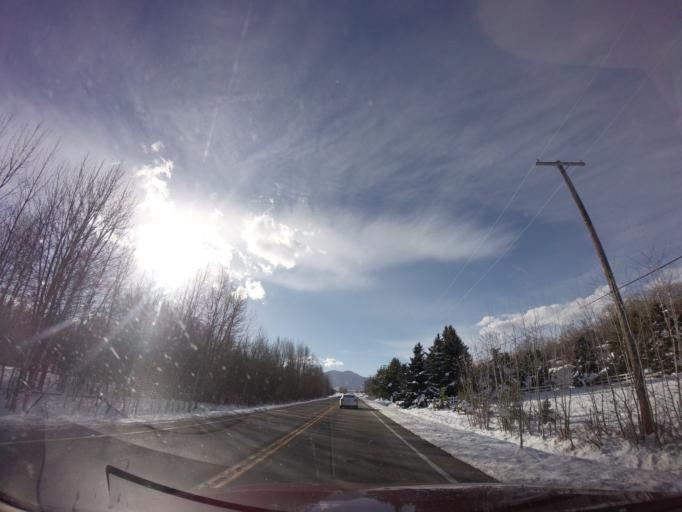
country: US
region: Montana
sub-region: Carbon County
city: Red Lodge
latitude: 45.2159
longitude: -109.2421
